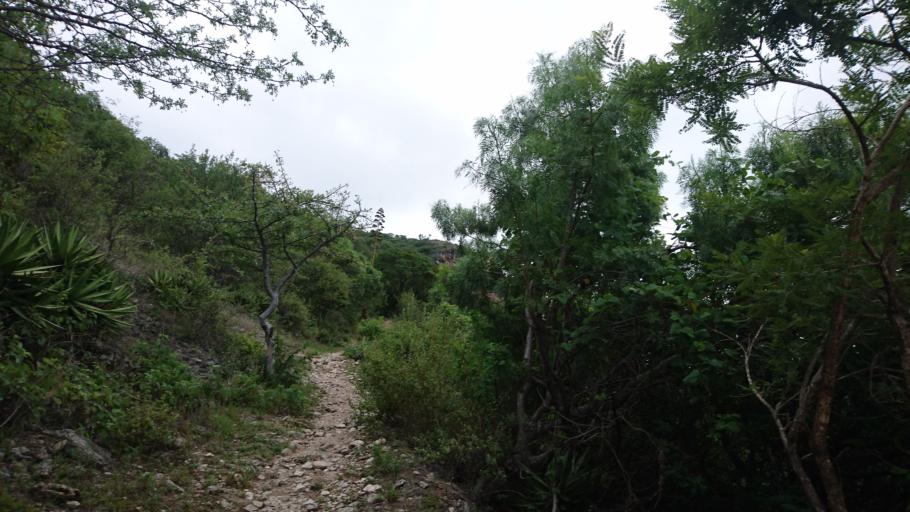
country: MX
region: Oaxaca
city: San Lorenzo Albarradas
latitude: 16.8656
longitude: -96.2746
